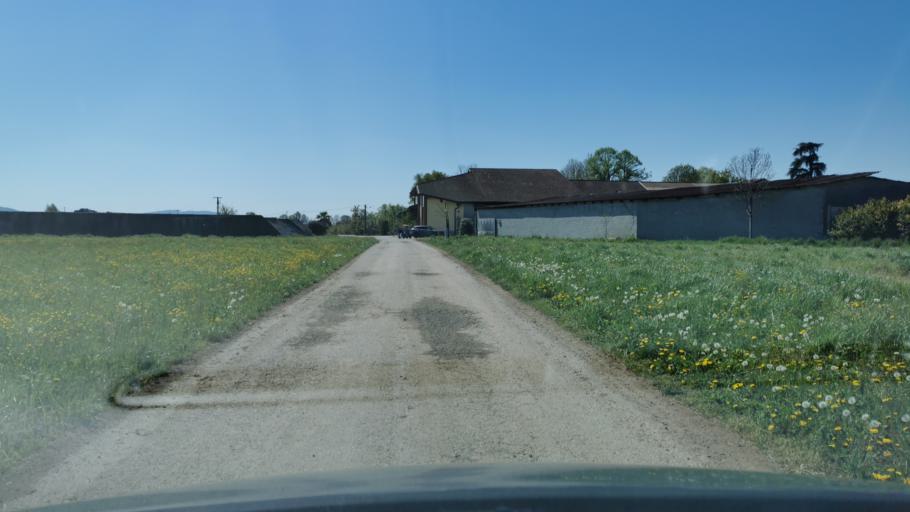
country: IT
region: Piedmont
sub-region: Provincia di Torino
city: Lombardore
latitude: 45.2163
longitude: 7.7107
